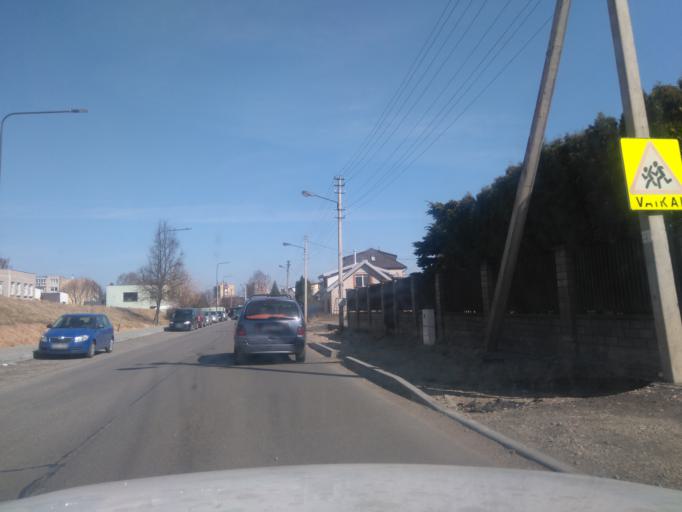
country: LT
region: Kauno apskritis
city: Dainava (Kaunas)
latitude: 54.8872
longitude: 23.9538
